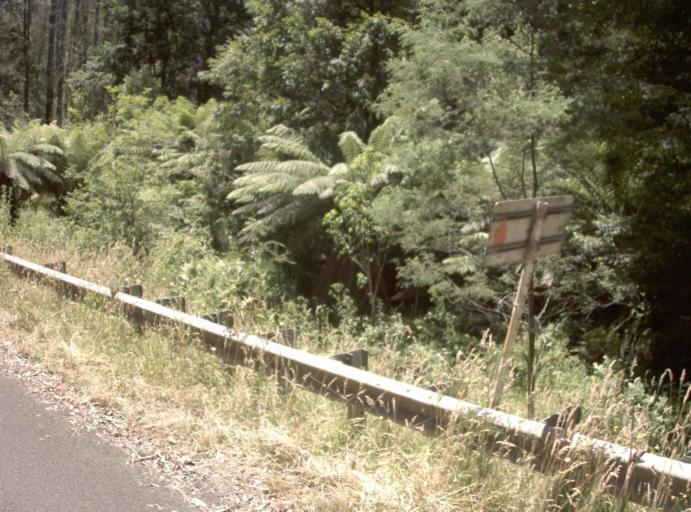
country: AU
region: Victoria
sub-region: Yarra Ranges
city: Millgrove
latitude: -37.6465
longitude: 145.7247
